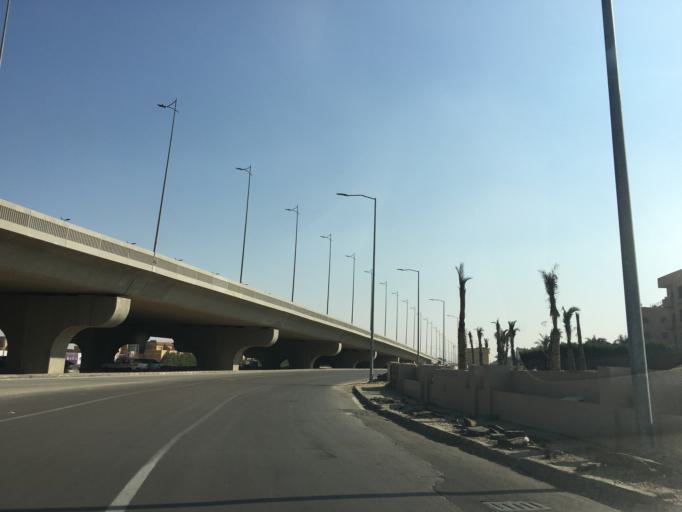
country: EG
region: Al Jizah
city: Awsim
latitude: 30.0078
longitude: 30.9821
